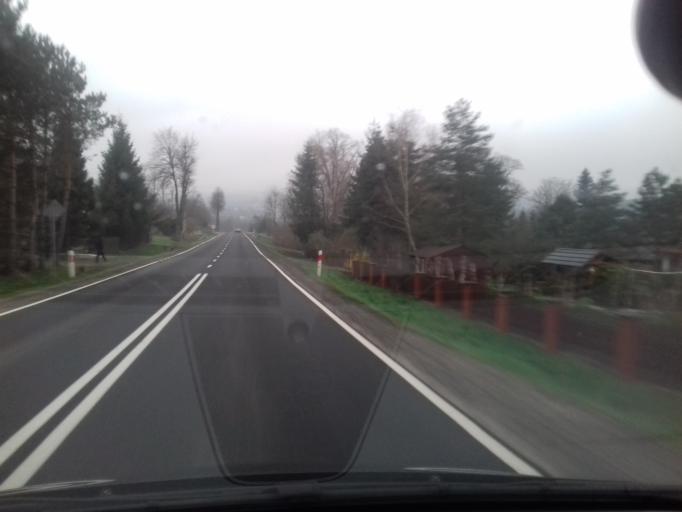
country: PL
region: Lesser Poland Voivodeship
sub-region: Powiat limanowski
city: Dobra
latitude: 49.7082
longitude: 20.2447
